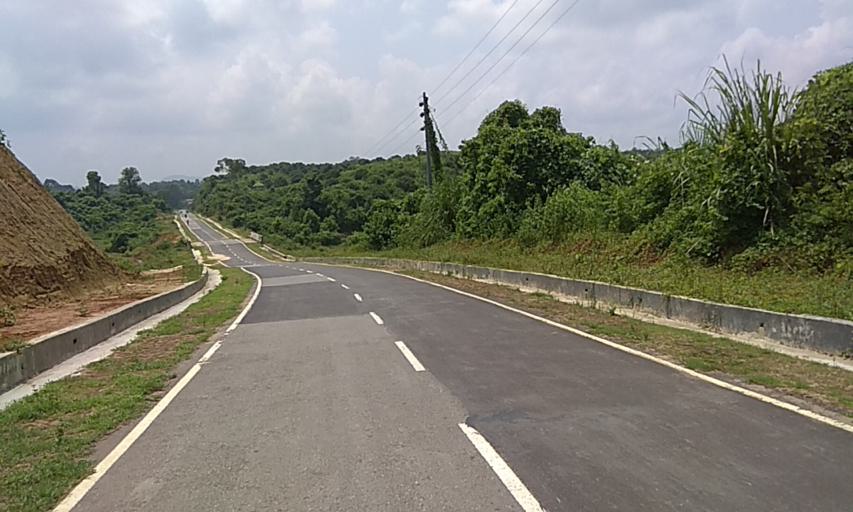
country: BD
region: Chittagong
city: Manikchari
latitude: 22.9380
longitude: 91.9043
